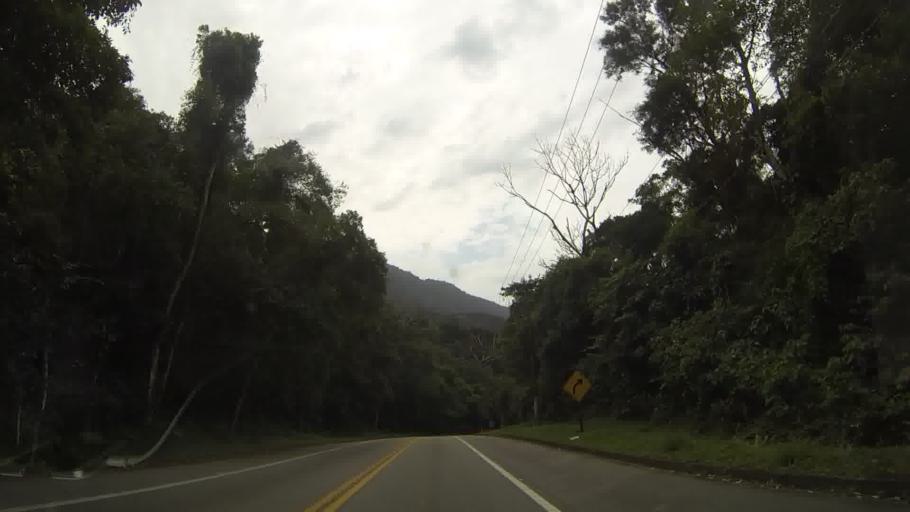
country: BR
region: Sao Paulo
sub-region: Sao Sebastiao
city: Sao Sebastiao
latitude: -23.8202
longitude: -45.4767
